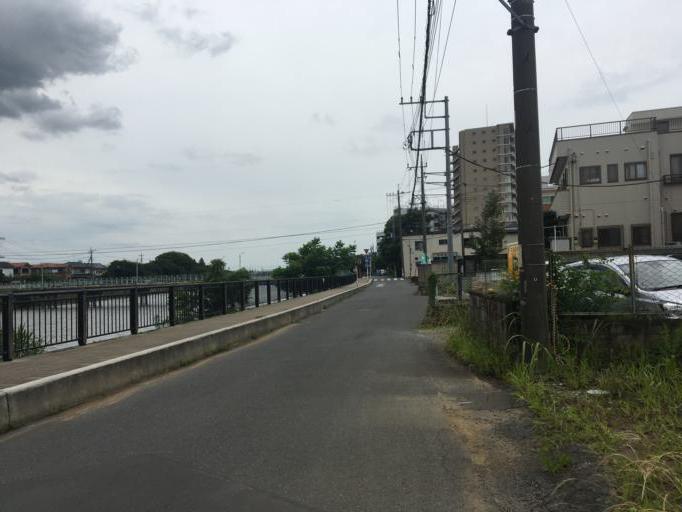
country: JP
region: Saitama
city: Kasukabe
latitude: 35.9829
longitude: 139.7558
